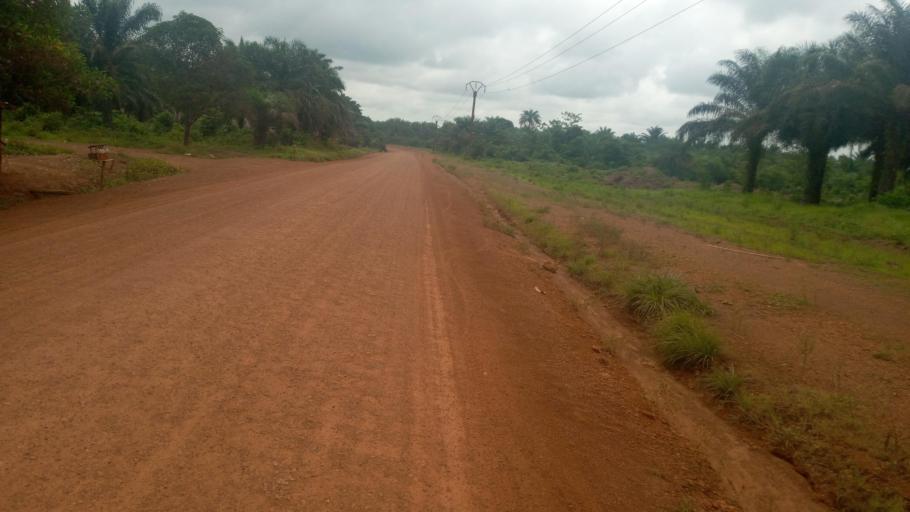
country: SL
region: Southern Province
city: Mogbwemo
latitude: 7.7248
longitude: -12.2803
